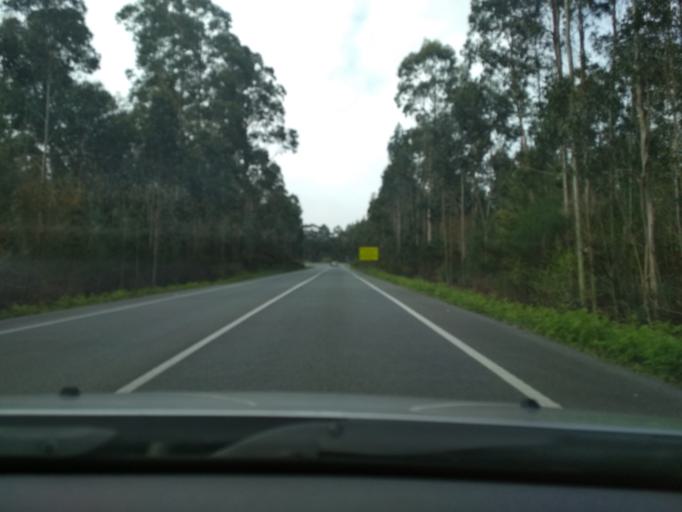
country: ES
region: Galicia
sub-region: Provincia de Pontevedra
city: Catoira
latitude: 42.6567
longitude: -8.7037
